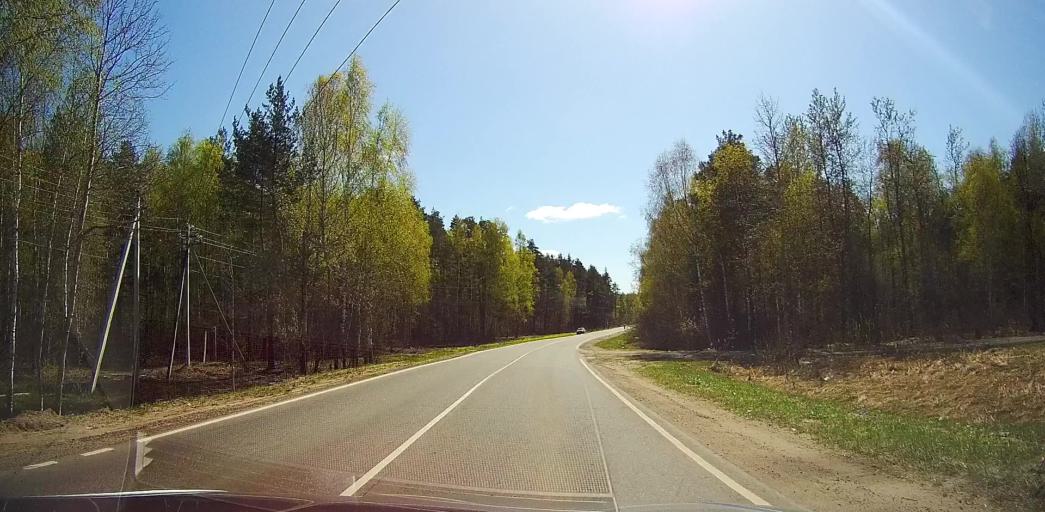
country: RU
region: Moskovskaya
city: Beloozerskiy
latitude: 55.5016
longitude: 38.4310
